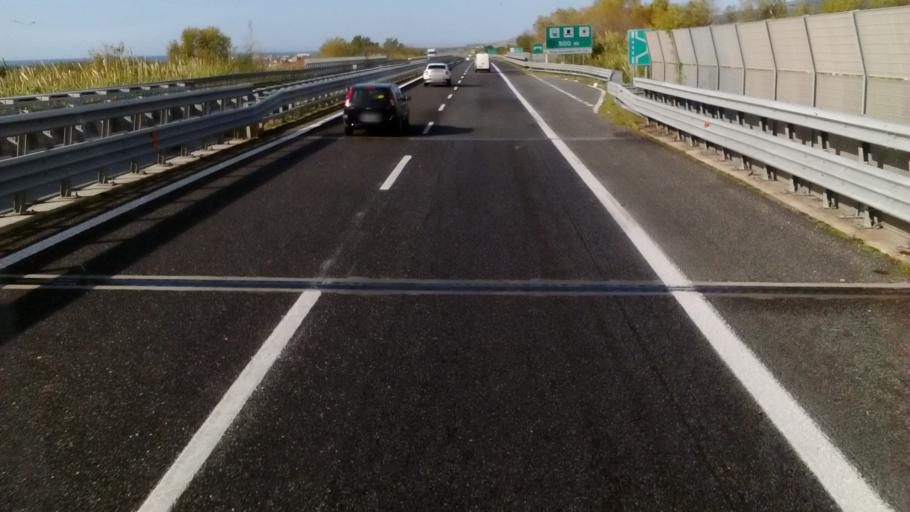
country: IT
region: Calabria
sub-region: Provincia di Catanzaro
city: Santa Eufemia Lamezia
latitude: 38.9275
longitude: 16.2453
